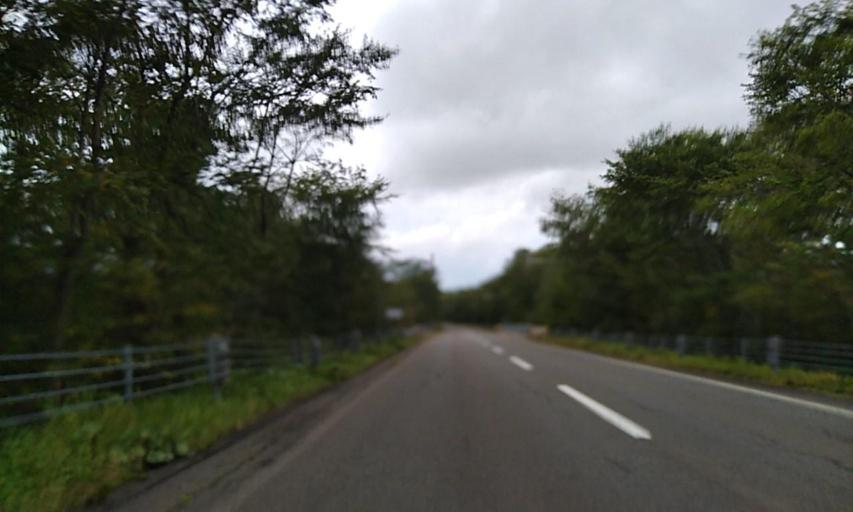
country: JP
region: Hokkaido
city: Bihoro
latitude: 43.5178
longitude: 144.4241
